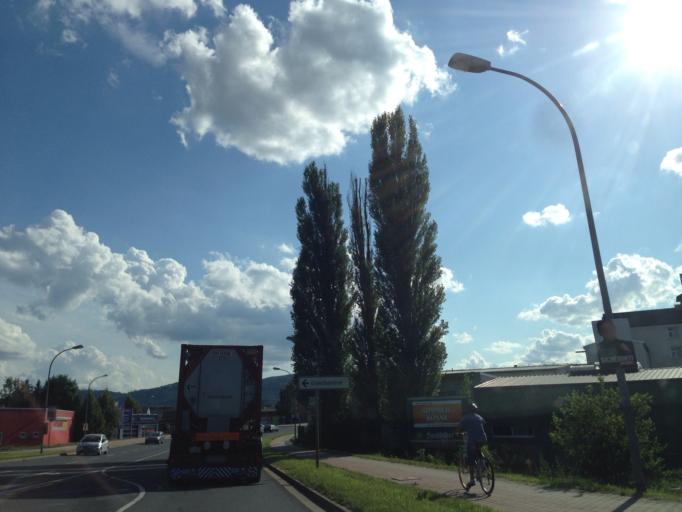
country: DE
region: Thuringia
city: Saalfeld
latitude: 50.6555
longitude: 11.3784
